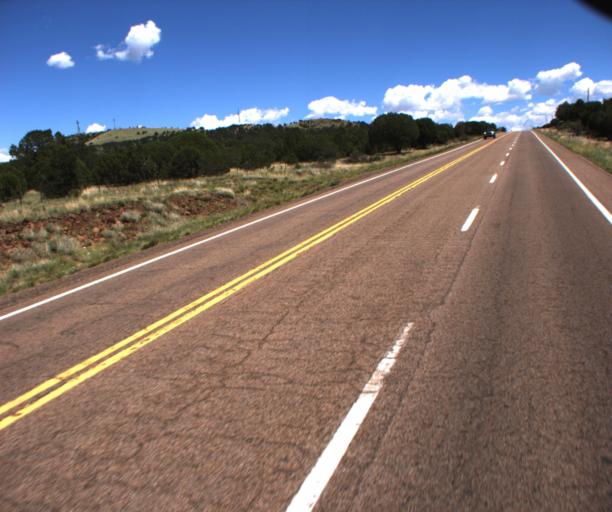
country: US
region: Arizona
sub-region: Apache County
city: Saint Johns
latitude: 34.2679
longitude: -109.5907
